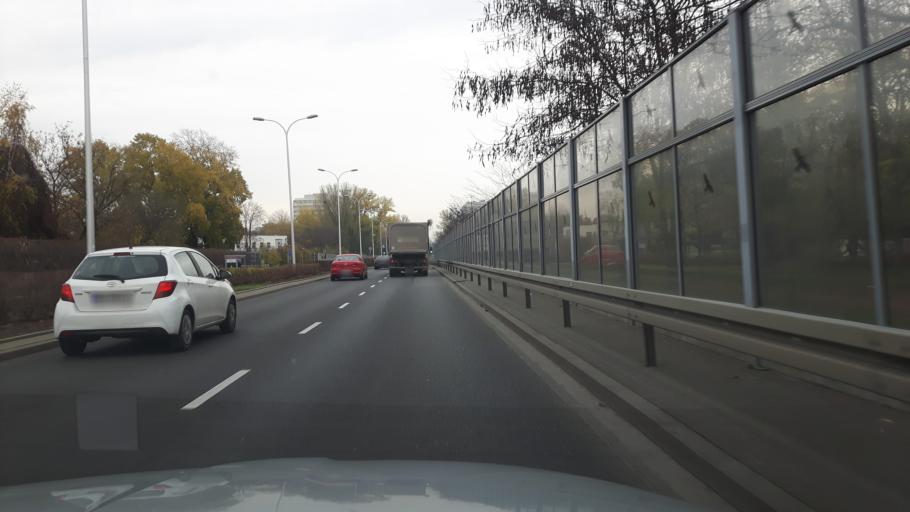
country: PL
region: Masovian Voivodeship
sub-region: Warszawa
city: Ursynow
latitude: 52.1716
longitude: 21.0590
